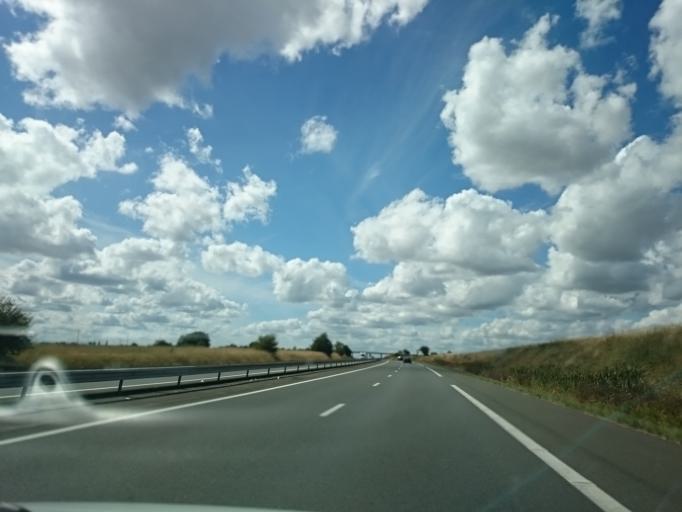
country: FR
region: Pays de la Loire
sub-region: Departement de Maine-et-Loire
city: Saint-Germain-des-Pres
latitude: 47.4374
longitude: -0.8346
